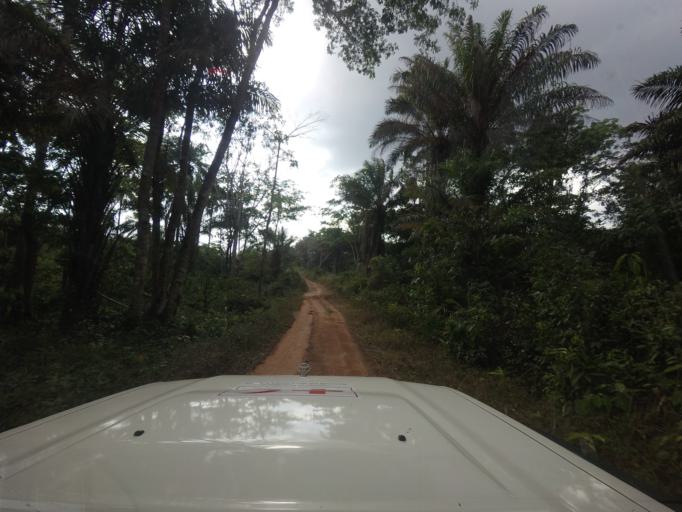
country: LR
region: Lofa
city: Voinjama
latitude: 8.3952
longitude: -9.6321
